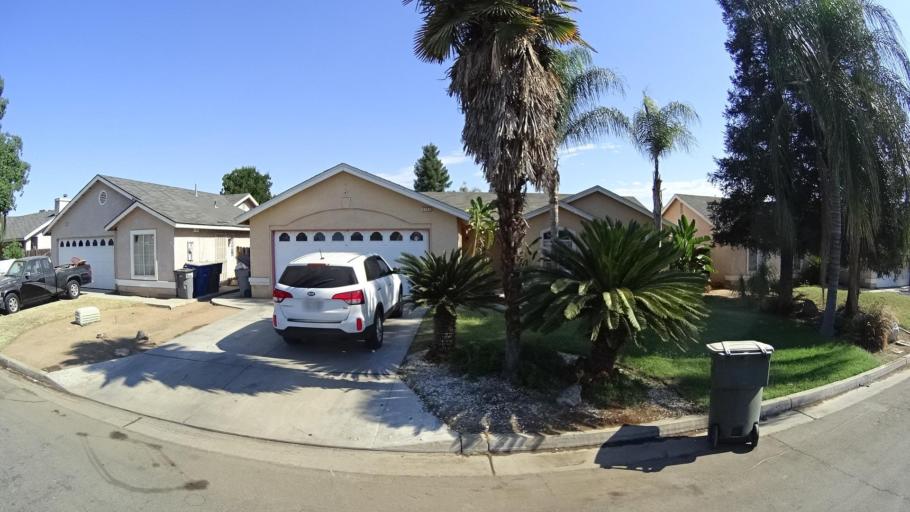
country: US
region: California
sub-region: Fresno County
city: Sunnyside
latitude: 36.7155
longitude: -119.7207
